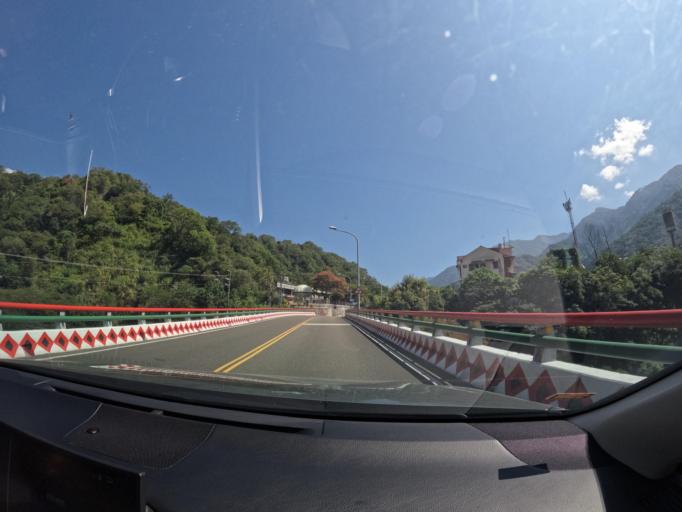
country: TW
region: Taiwan
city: Yujing
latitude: 23.1581
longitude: 120.7631
